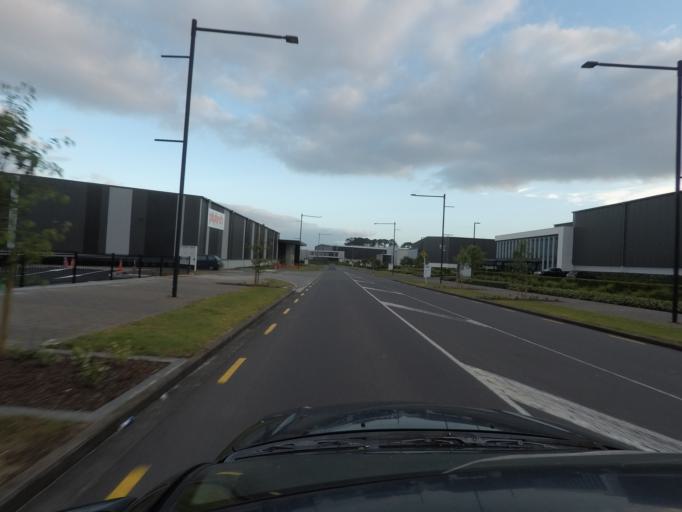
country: NZ
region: Auckland
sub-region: Auckland
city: Tamaki
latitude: -36.9355
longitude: 174.8761
